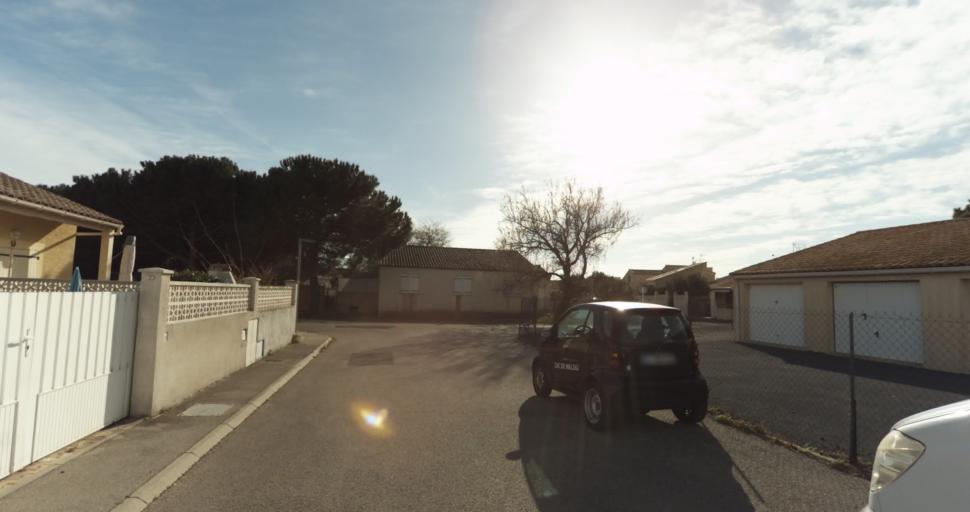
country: FR
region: Languedoc-Roussillon
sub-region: Departement de l'Herault
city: Marseillan
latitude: 43.3160
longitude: 3.5393
